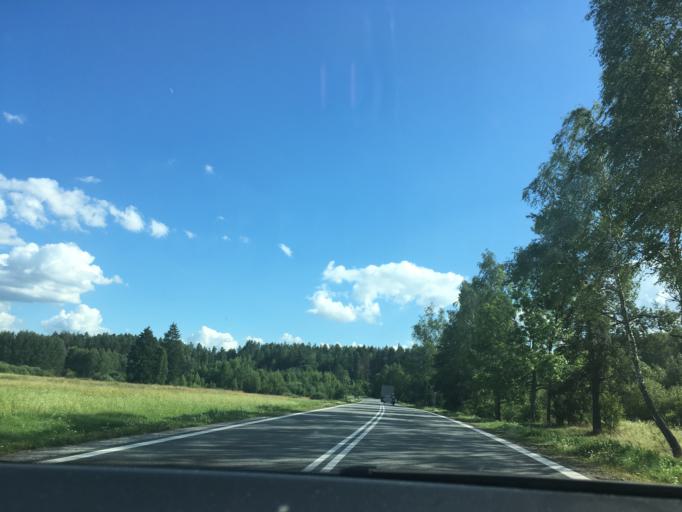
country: PL
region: Podlasie
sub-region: Powiat bialostocki
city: Wasilkow
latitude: 53.2735
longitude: 23.1199
